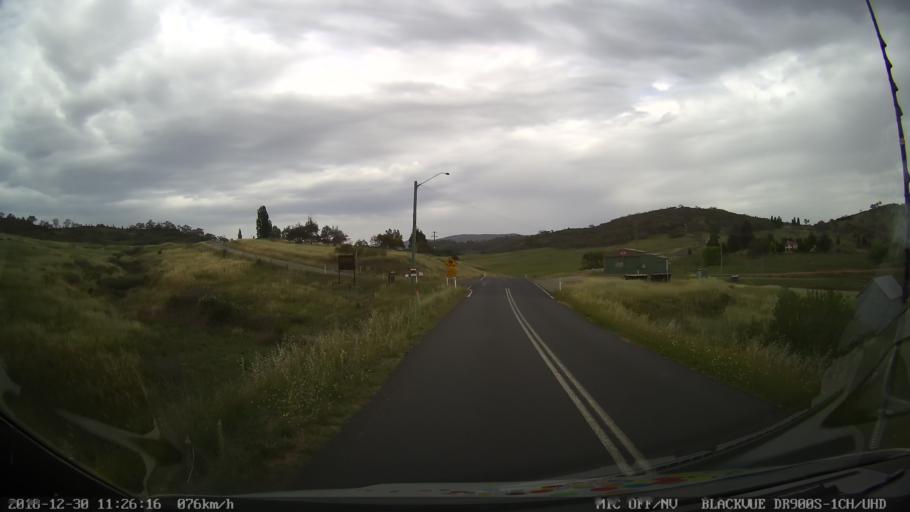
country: AU
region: New South Wales
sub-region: Snowy River
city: Jindabyne
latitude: -36.4694
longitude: 148.6361
